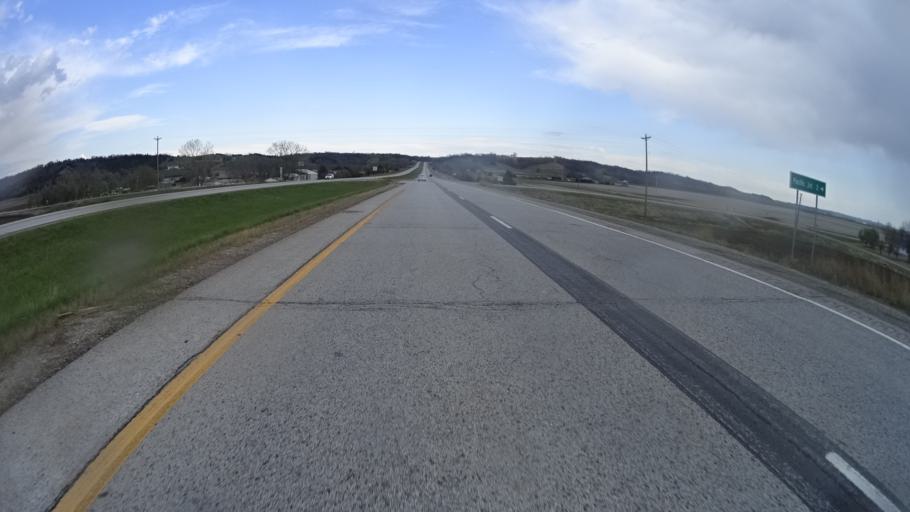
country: US
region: Iowa
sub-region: Mills County
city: Glenwood
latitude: 41.0462
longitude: -95.8055
